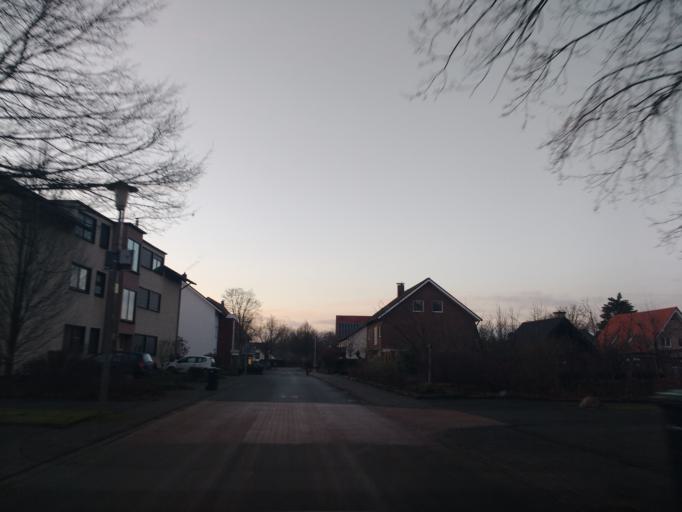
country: DE
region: North Rhine-Westphalia
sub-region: Regierungsbezirk Detmold
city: Hovelhof
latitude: 51.8491
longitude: 8.6256
